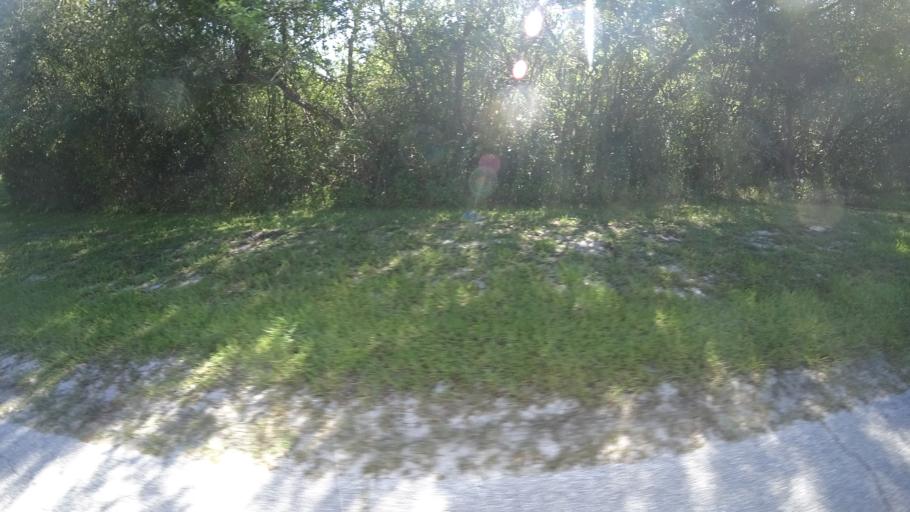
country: US
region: Florida
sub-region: Sarasota County
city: The Meadows
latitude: 27.4227
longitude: -82.3493
